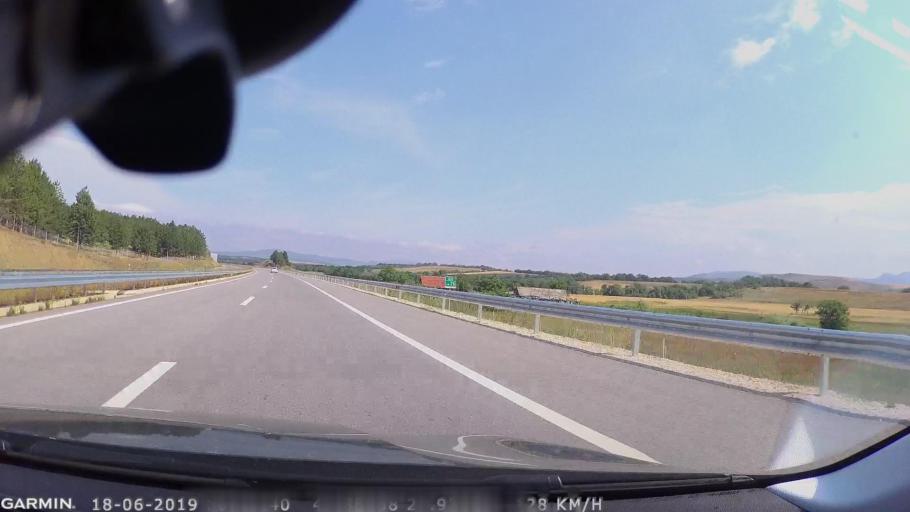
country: MK
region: Sveti Nikole
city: Sveti Nikole
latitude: 41.8864
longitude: 21.9326
